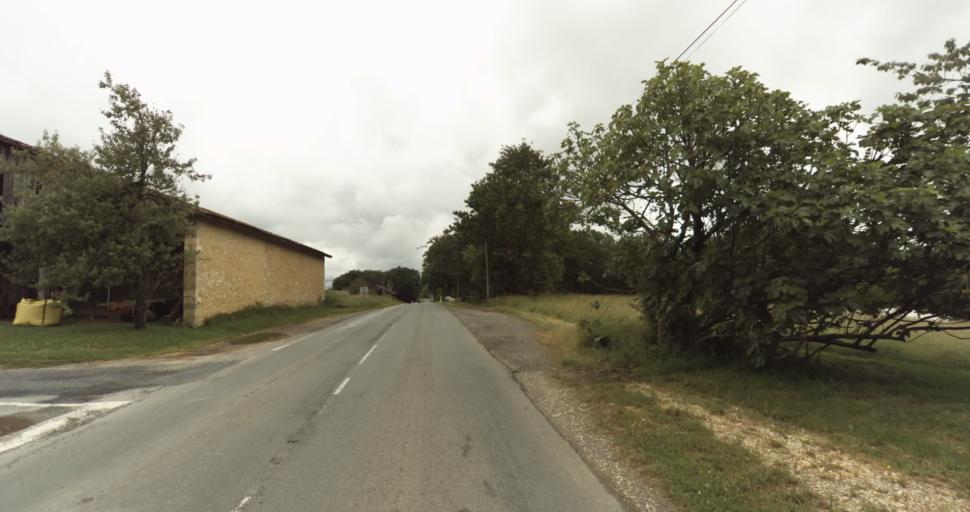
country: FR
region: Aquitaine
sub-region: Departement de la Dordogne
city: Beaumont-du-Perigord
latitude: 44.7270
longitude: 0.7914
